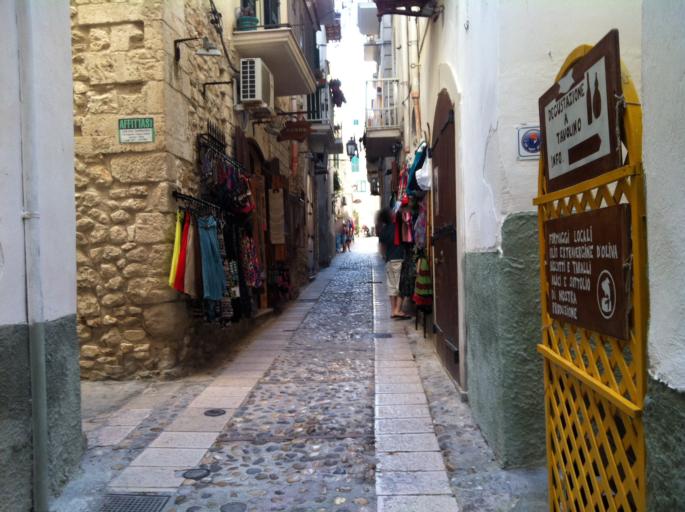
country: IT
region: Apulia
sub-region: Provincia di Foggia
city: Vieste
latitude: 41.8827
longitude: 16.1824
